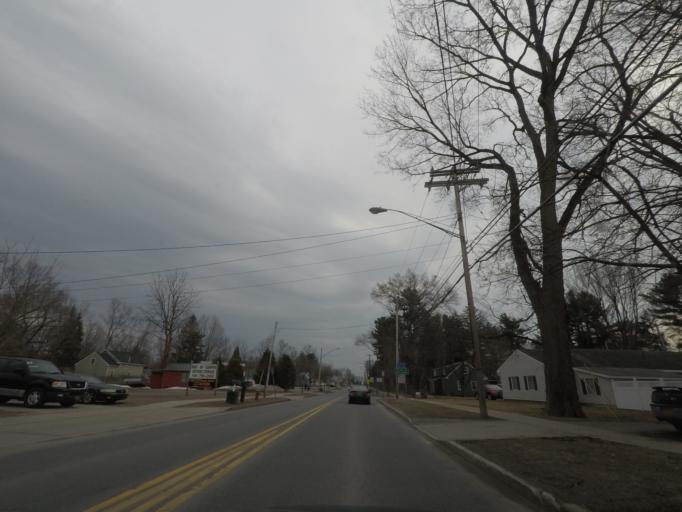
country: US
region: New York
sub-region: Washington County
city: Fort Edward
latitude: 43.2794
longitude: -73.5864
